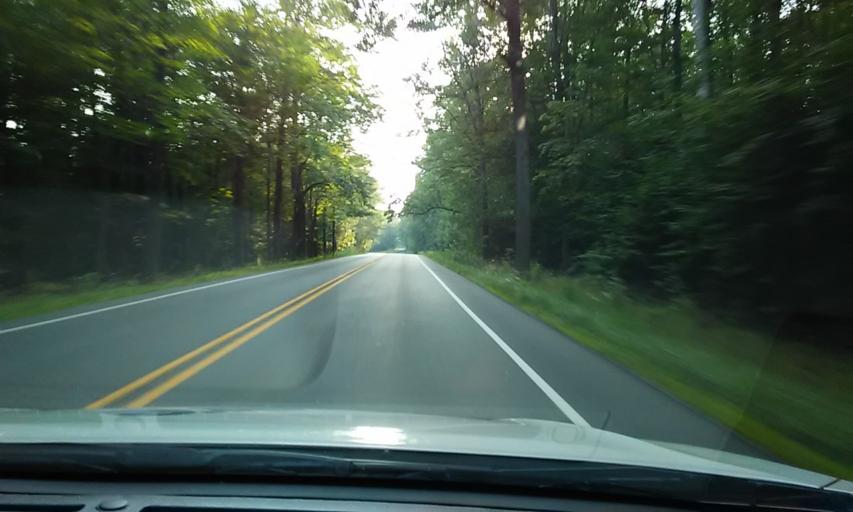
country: US
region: Pennsylvania
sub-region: Warren County
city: Sheffield
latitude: 41.5793
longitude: -78.9492
